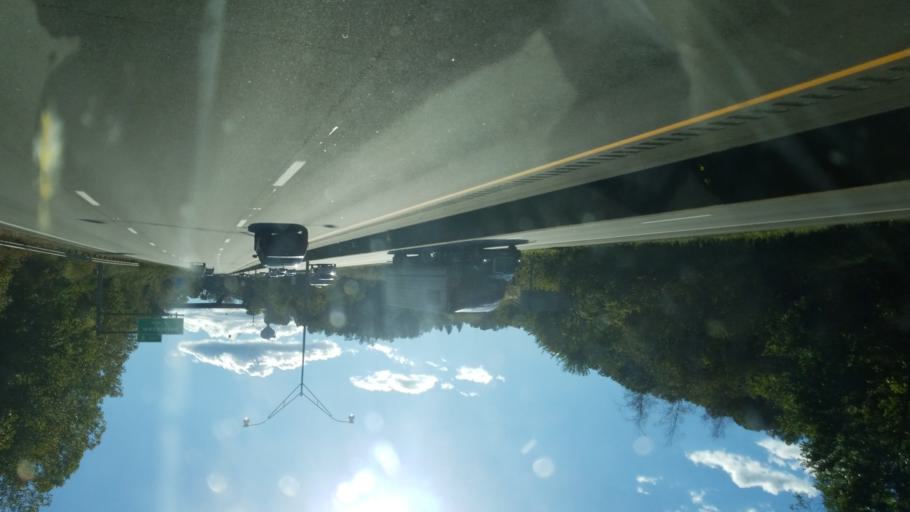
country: US
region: West Virginia
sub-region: Ohio County
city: Bethlehem
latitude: 40.0502
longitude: -80.6836
